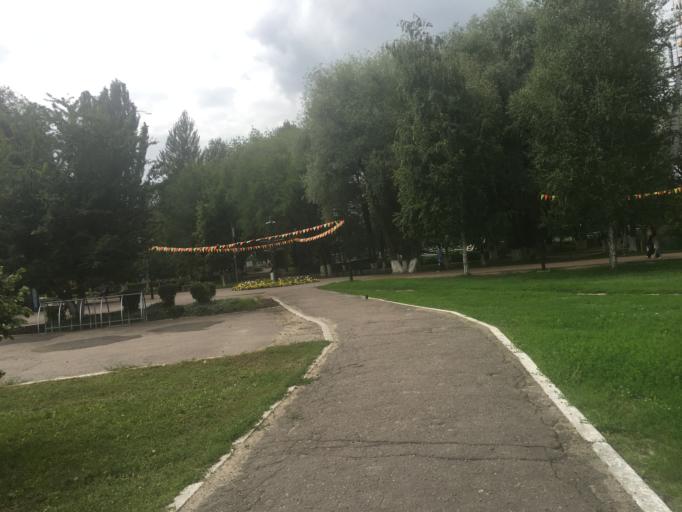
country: RU
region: Voronezj
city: Rossosh'
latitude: 50.1957
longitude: 39.5768
